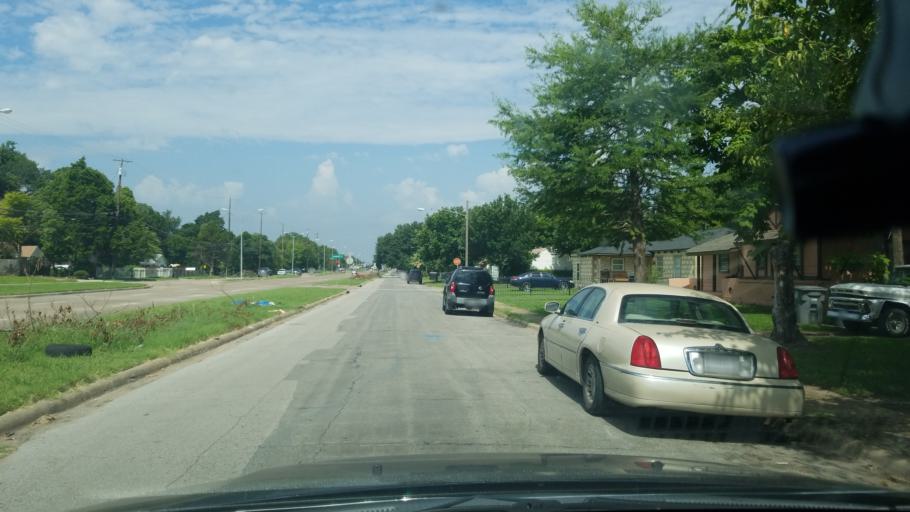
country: US
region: Texas
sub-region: Dallas County
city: Balch Springs
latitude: 32.7345
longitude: -96.6924
